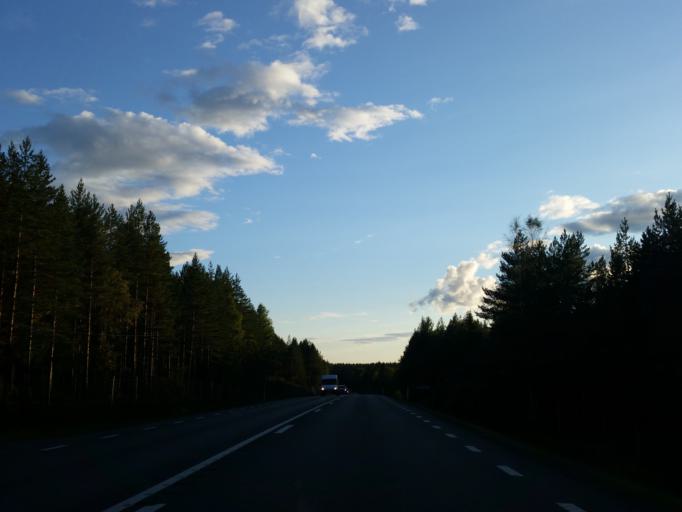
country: SE
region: Vaesterbotten
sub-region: Robertsfors Kommun
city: Robertsfors
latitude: 64.0155
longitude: 20.8264
